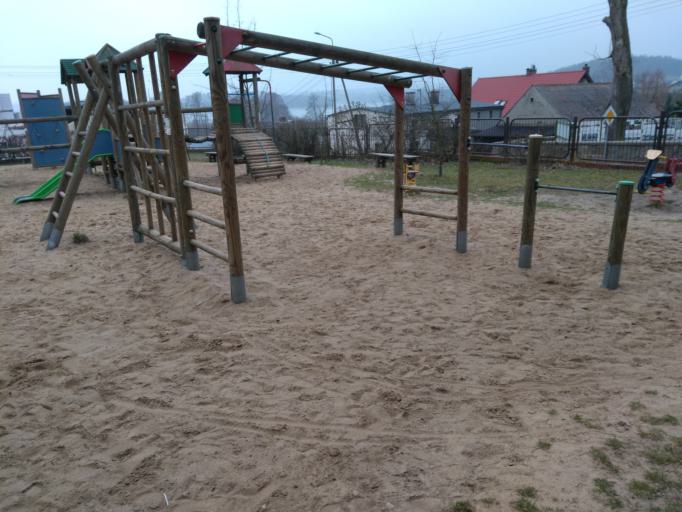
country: PL
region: Pomeranian Voivodeship
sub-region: Powiat kartuski
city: Suleczyno
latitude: 54.3239
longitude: 17.7983
